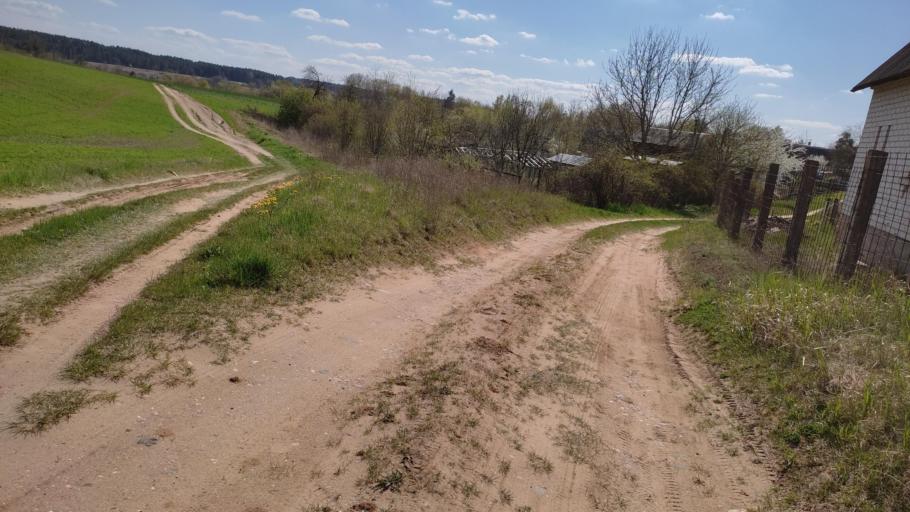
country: BY
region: Grodnenskaya
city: Hrodna
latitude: 53.6574
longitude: 23.9060
